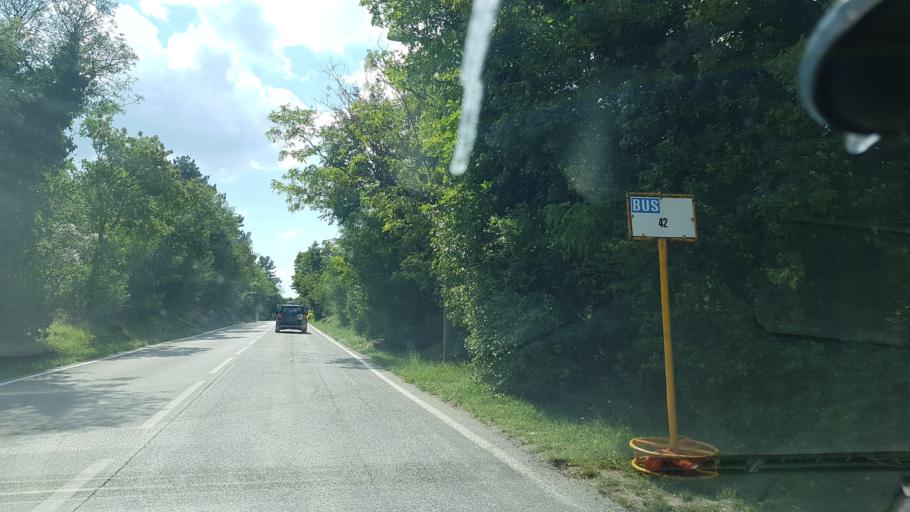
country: IT
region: Friuli Venezia Giulia
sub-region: Provincia di Trieste
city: Villa Opicina
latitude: 45.6958
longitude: 13.7976
